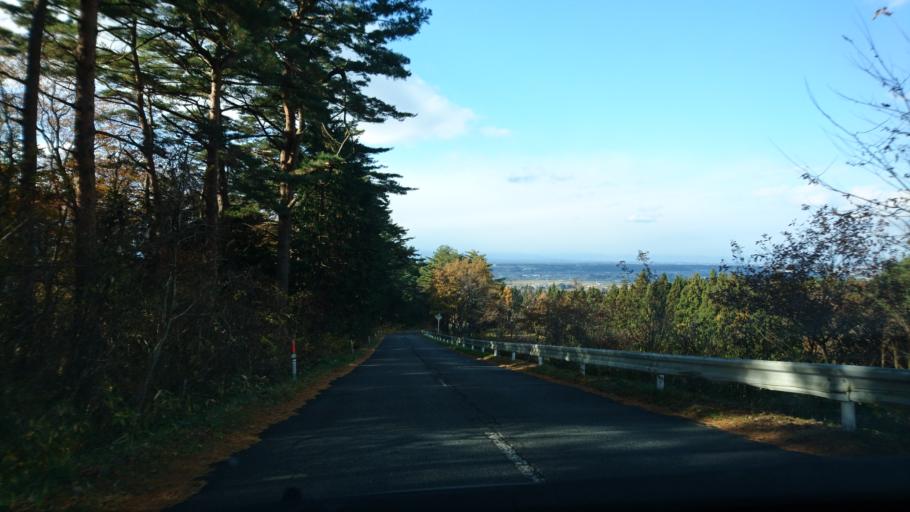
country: JP
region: Iwate
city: Mizusawa
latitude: 39.0286
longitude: 141.1643
